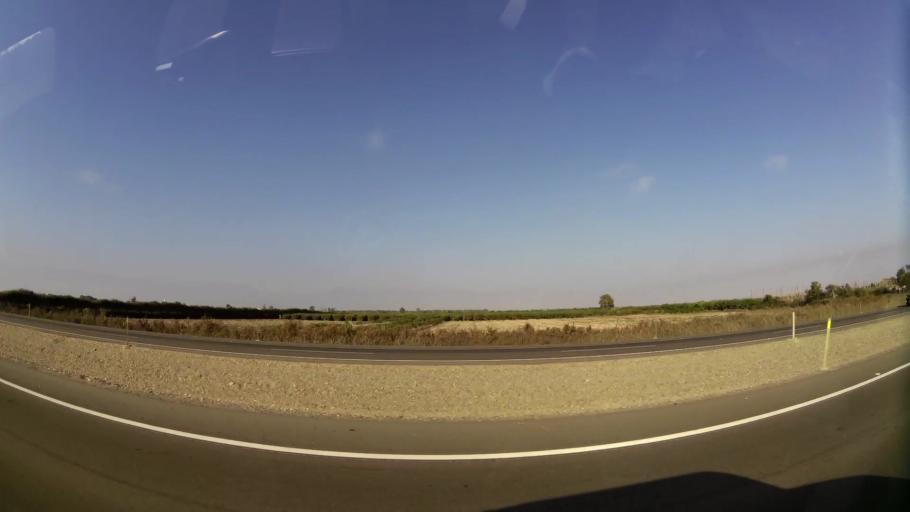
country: PE
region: Ica
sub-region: Provincia de Chincha
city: Chincha Baja
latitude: -13.4854
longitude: -76.1847
